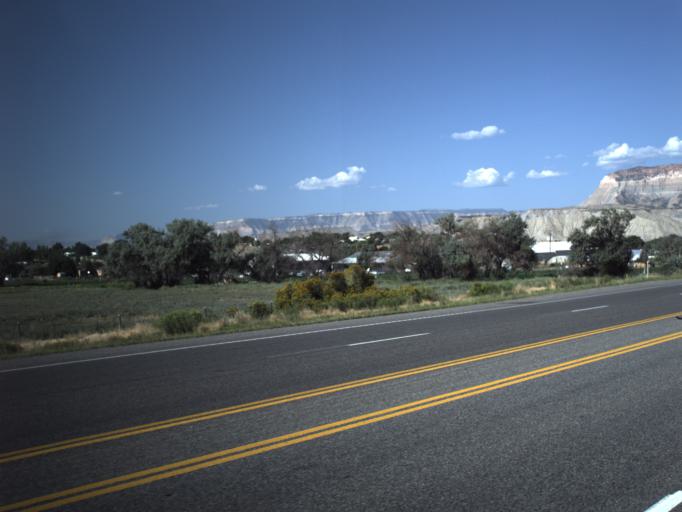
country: US
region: Utah
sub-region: Emery County
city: Huntington
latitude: 39.3393
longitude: -110.9512
